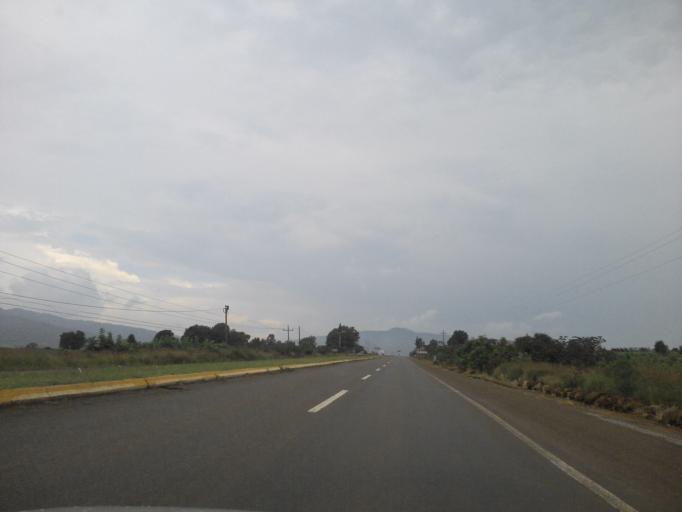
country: MX
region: Jalisco
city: San Jose de Gracia
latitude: 20.7379
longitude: -102.5114
